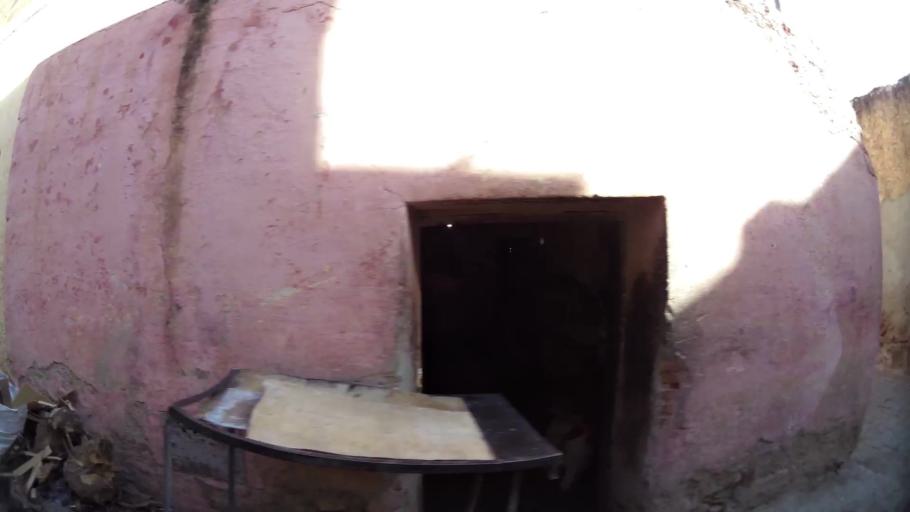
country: MA
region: Oriental
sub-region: Oujda-Angad
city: Oujda
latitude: 34.6732
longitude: -1.8980
